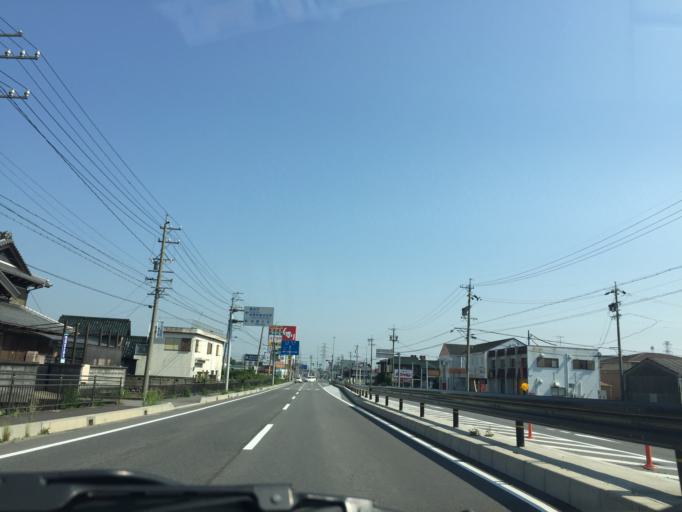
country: JP
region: Aichi
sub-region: Tsushima-shi
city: Tsushima
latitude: 35.1301
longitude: 136.6481
